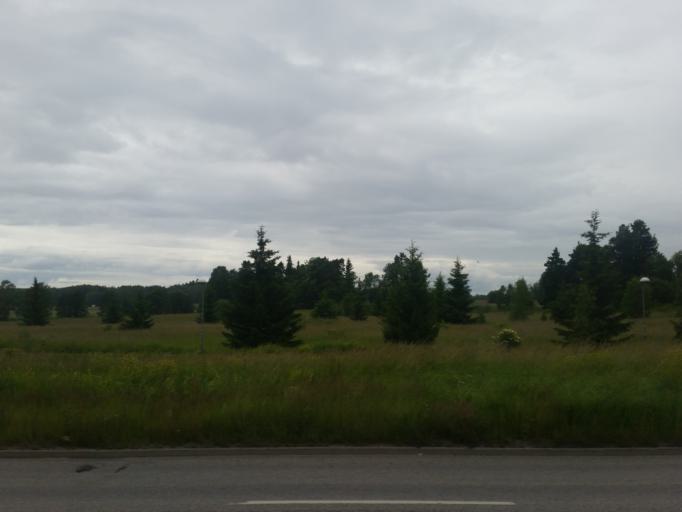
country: SE
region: Stockholm
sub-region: Stockholms Kommun
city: Kista
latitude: 59.4125
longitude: 17.8990
